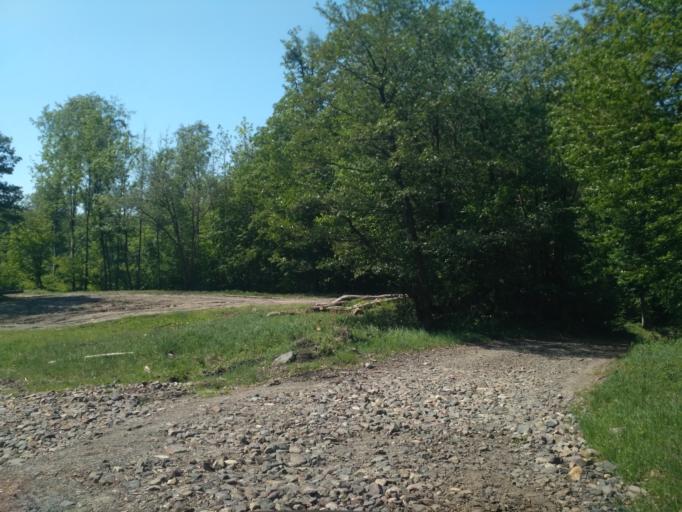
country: SK
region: Presovsky
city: Vranov nad Topl'ou
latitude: 48.8404
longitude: 21.4780
